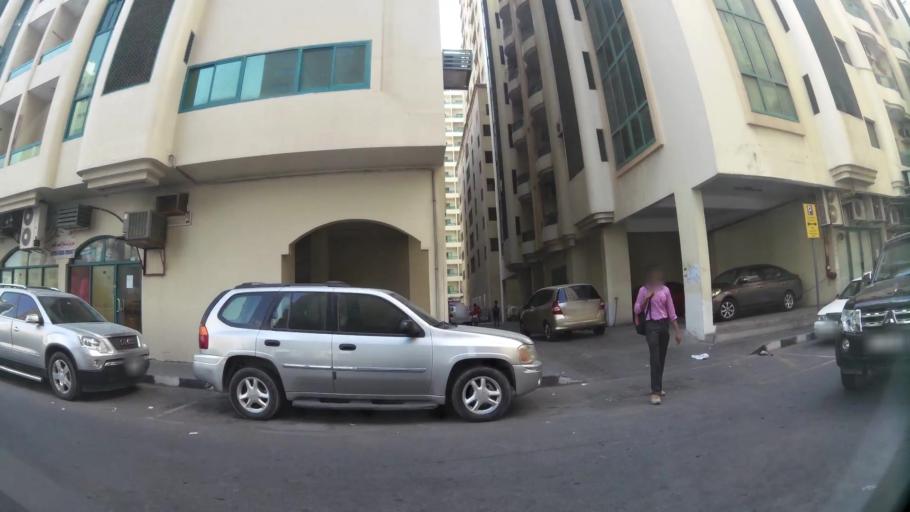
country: AE
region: Ash Shariqah
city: Sharjah
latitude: 25.3445
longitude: 55.3925
